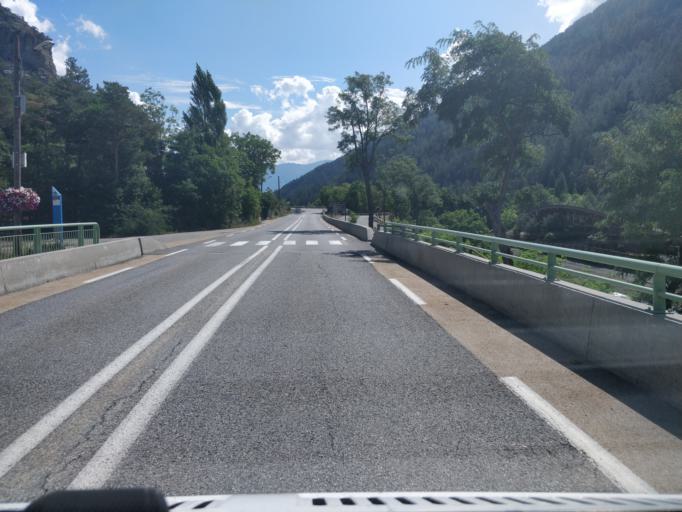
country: FR
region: Provence-Alpes-Cote d'Azur
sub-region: Departement des Alpes-de-Haute-Provence
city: Barcelonnette
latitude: 44.4016
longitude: 6.5120
